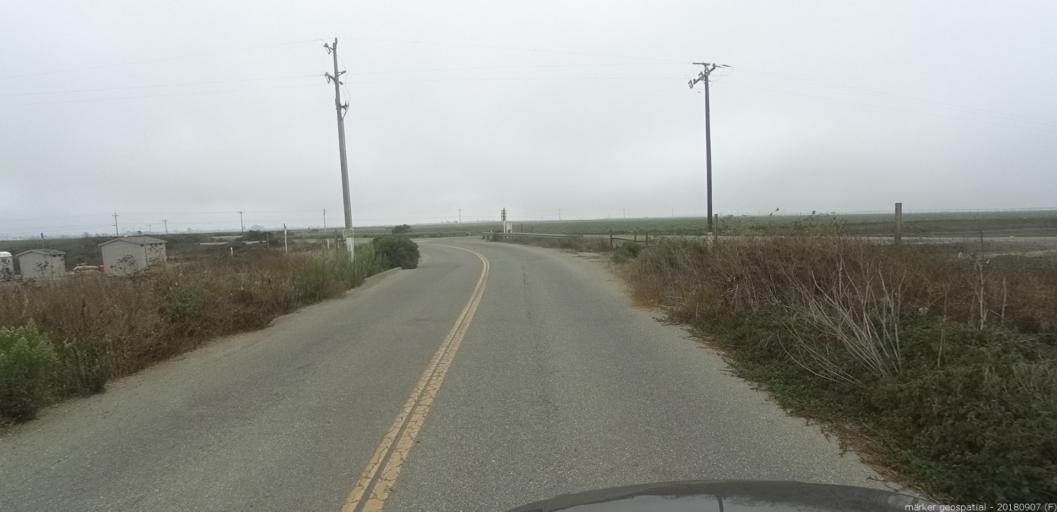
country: US
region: California
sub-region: Monterey County
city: Castroville
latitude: 36.7722
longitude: -121.7909
